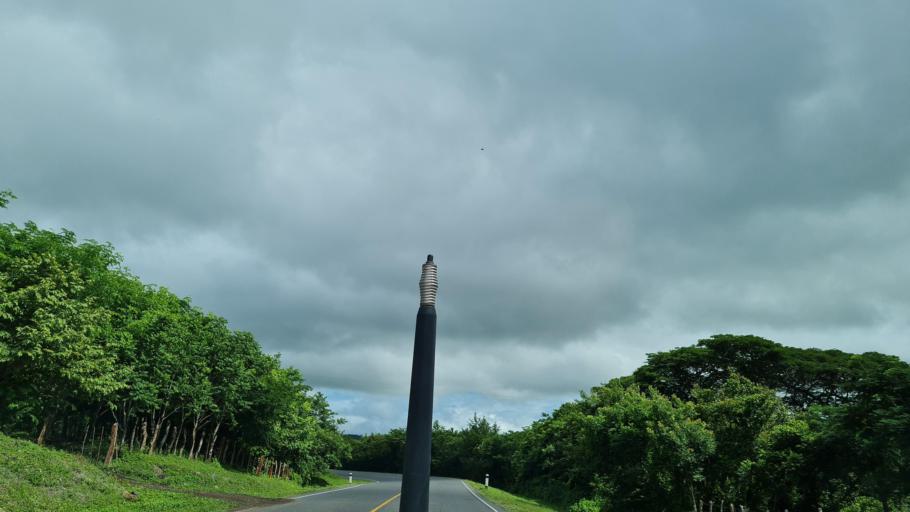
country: NI
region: Matagalpa
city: Terrabona
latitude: 12.5908
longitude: -85.9157
